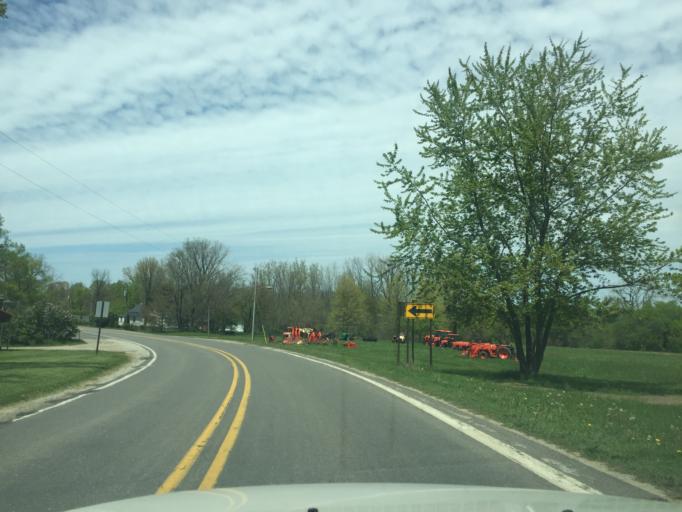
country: US
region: Michigan
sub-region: Berrien County
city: Stevensville
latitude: 41.9620
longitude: -86.4866
